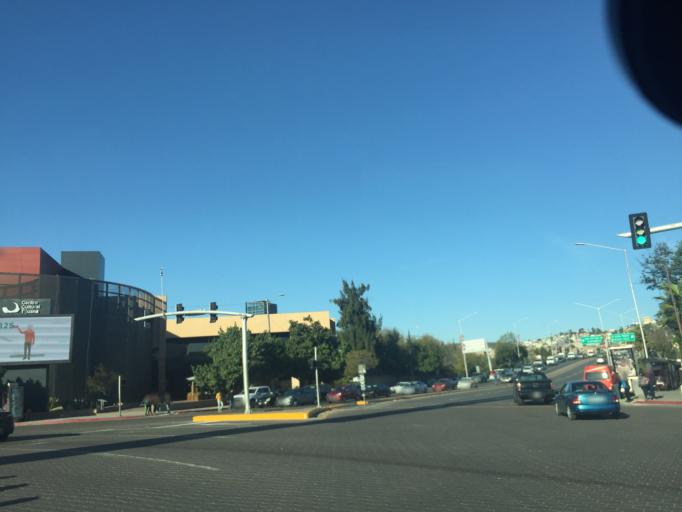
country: MX
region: Baja California
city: Tijuana
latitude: 32.5287
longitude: -117.0229
